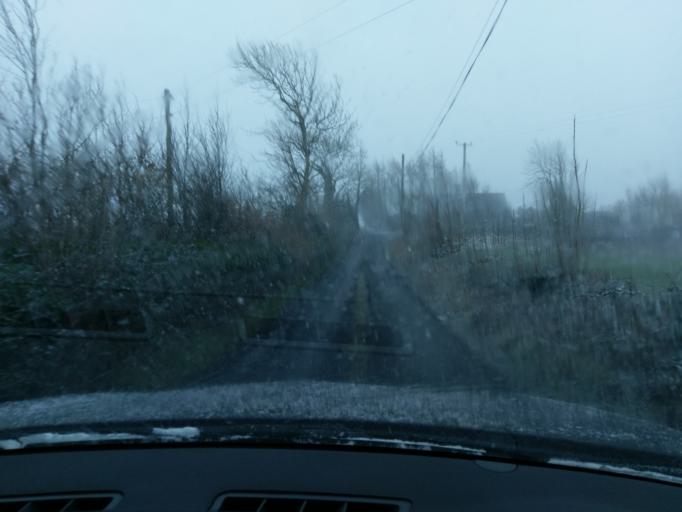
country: IE
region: Connaught
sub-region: County Galway
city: Oranmore
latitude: 53.2063
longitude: -8.8896
